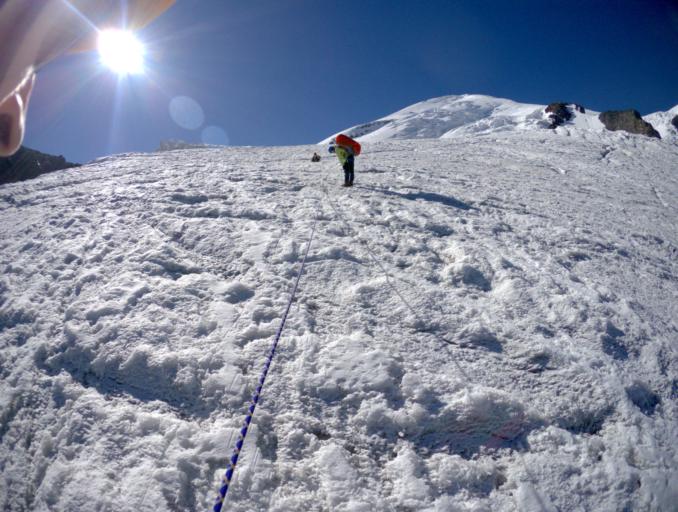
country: RU
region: Kabardino-Balkariya
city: Terskol
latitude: 43.3866
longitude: 42.4360
